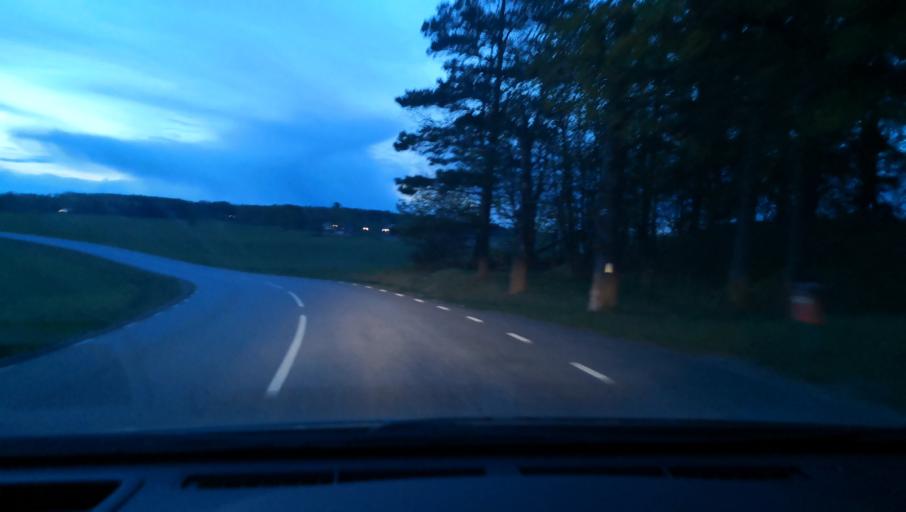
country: SE
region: OErebro
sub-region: Hallsbergs Kommun
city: Hallsberg
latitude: 59.1158
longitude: 15.0094
